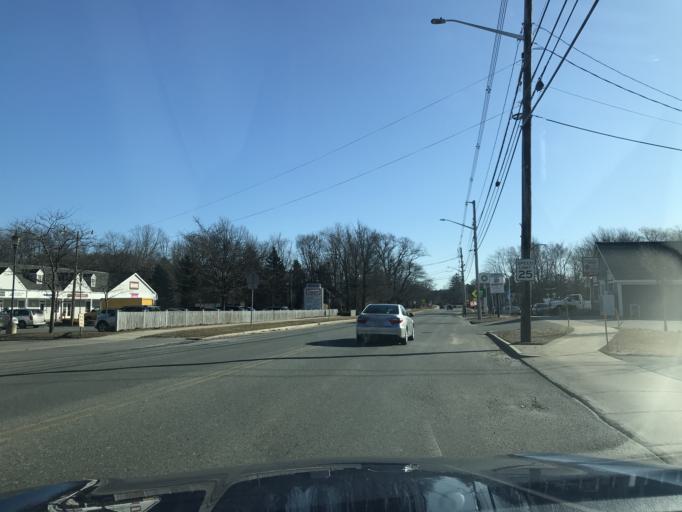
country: US
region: Massachusetts
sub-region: Essex County
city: Groveland
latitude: 42.7223
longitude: -70.9887
